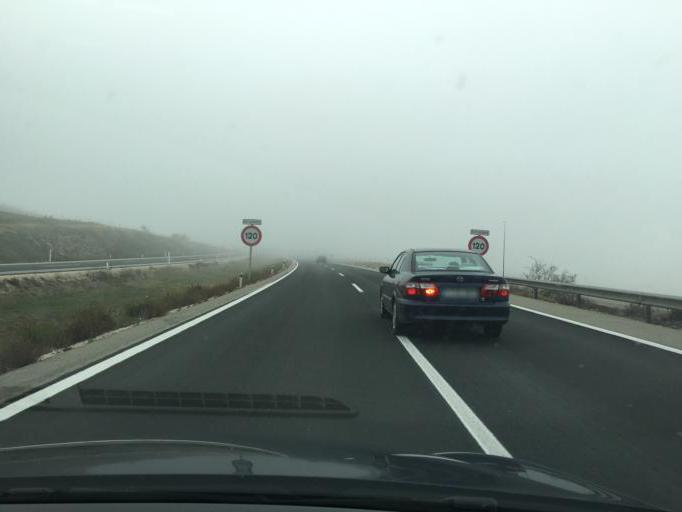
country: ES
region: Castille and Leon
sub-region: Provincia de Burgos
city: Pancorbo
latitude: 42.6238
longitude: -3.1380
